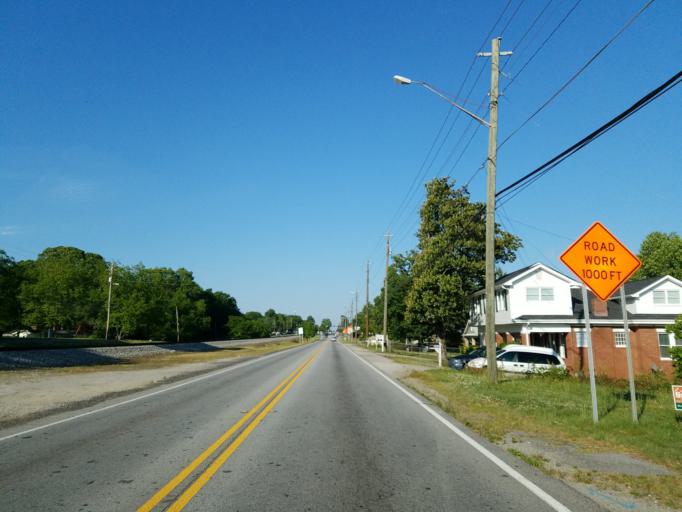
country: US
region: Georgia
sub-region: Douglas County
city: Douglasville
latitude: 33.7471
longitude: -84.7587
